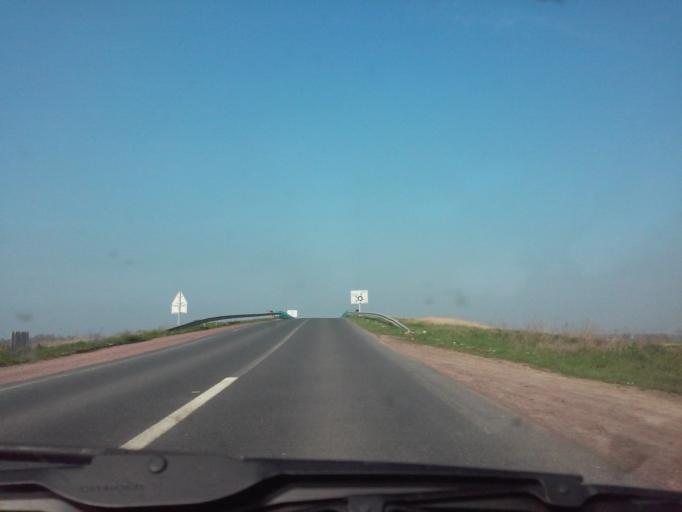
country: FR
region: Lower Normandy
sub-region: Departement du Calvados
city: Saint-Manvieu
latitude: 49.2192
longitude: -0.5423
